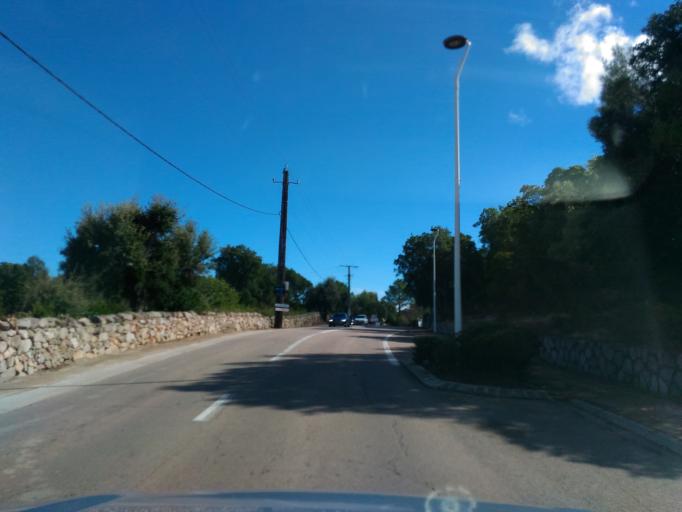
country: FR
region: Corsica
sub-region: Departement de la Corse-du-Sud
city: Porto-Vecchio
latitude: 41.6981
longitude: 9.3554
